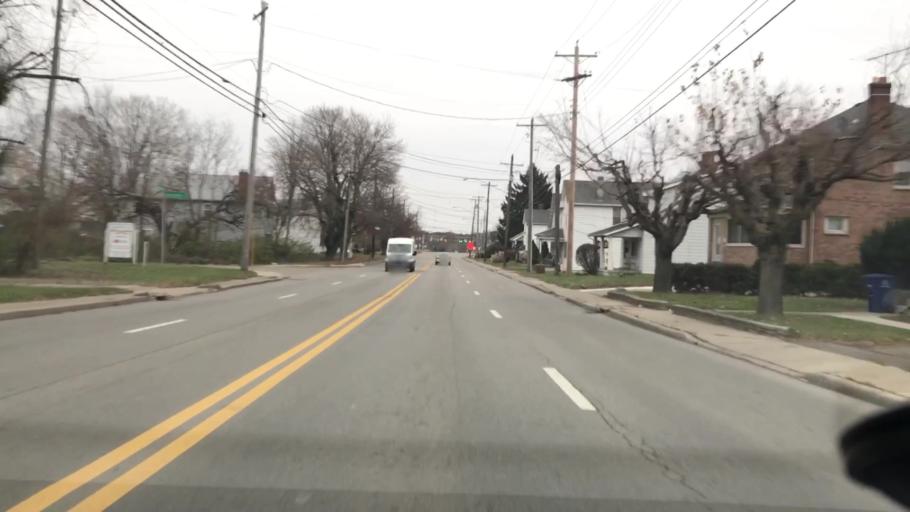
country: US
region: Ohio
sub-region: Franklin County
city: Upper Arlington
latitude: 39.9936
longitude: -83.0896
